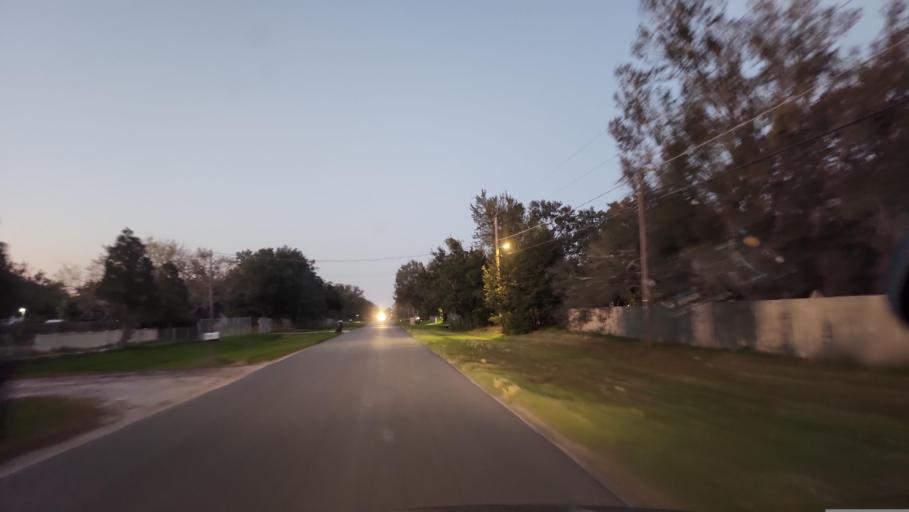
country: US
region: Florida
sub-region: Hillsborough County
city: Boyette
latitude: 27.8134
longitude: -82.2786
